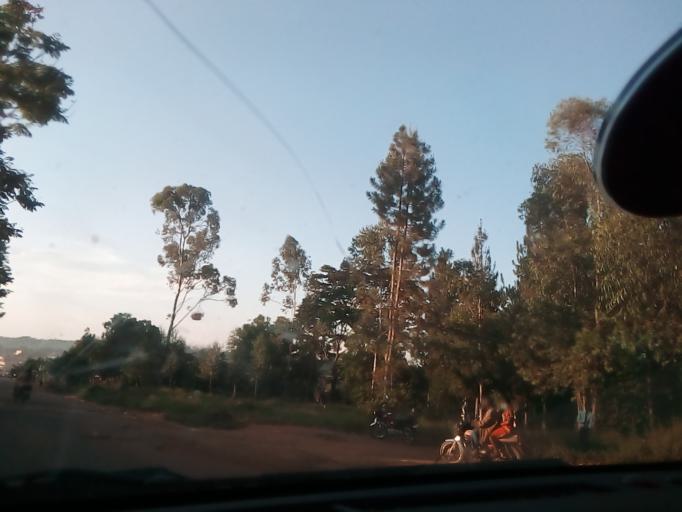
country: UG
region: Central Region
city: Masaka
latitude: -0.3299
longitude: 31.7610
